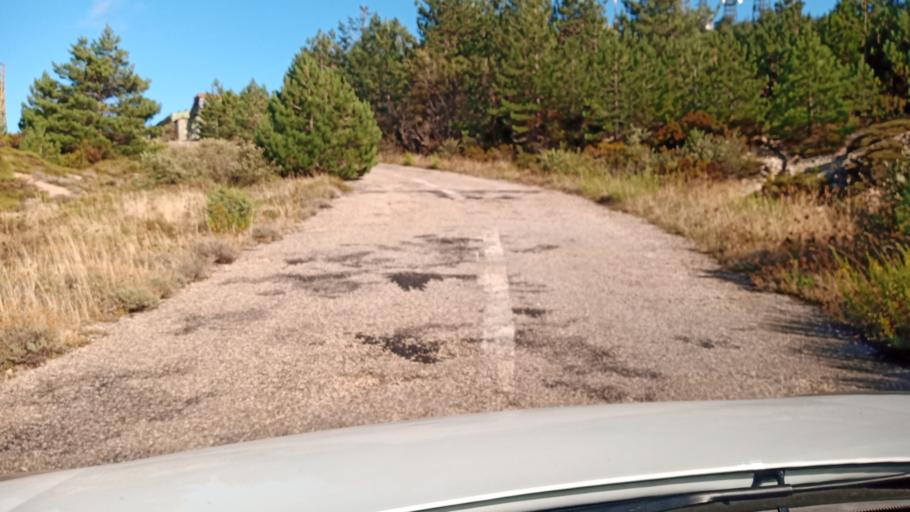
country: IT
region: Sardinia
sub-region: Provincia di Olbia-Tempio
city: Calangianus
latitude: 40.8568
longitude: 9.1682
